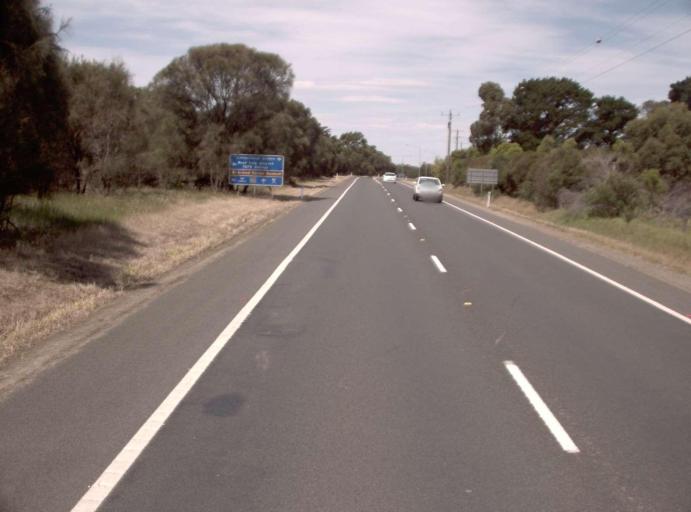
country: AU
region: Victoria
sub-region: Wellington
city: Sale
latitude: -38.0994
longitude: 146.9722
